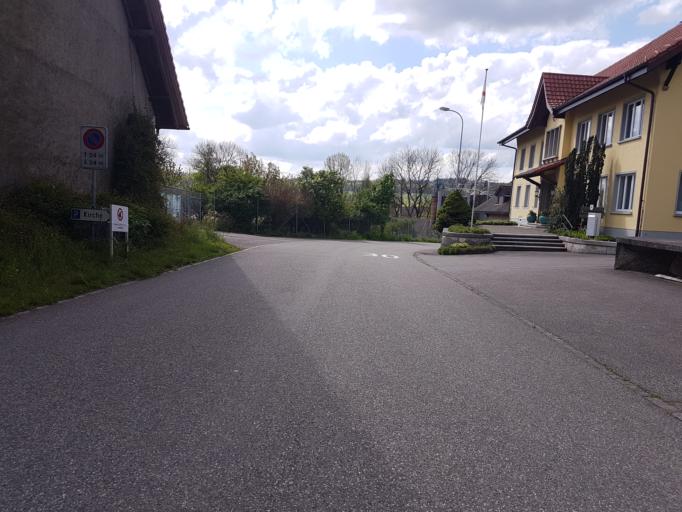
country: CH
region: Solothurn
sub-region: Bezirk Olten
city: Gunzgen
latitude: 47.3086
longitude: 7.8567
